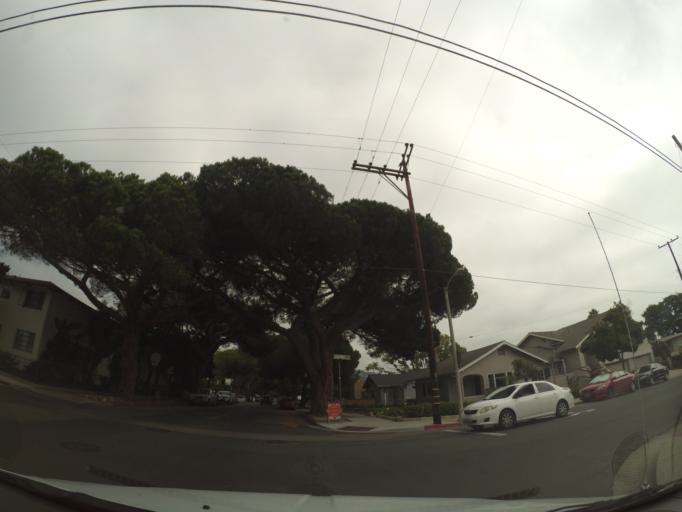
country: US
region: California
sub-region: Santa Barbara County
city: Santa Barbara
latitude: 34.4275
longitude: -119.7001
